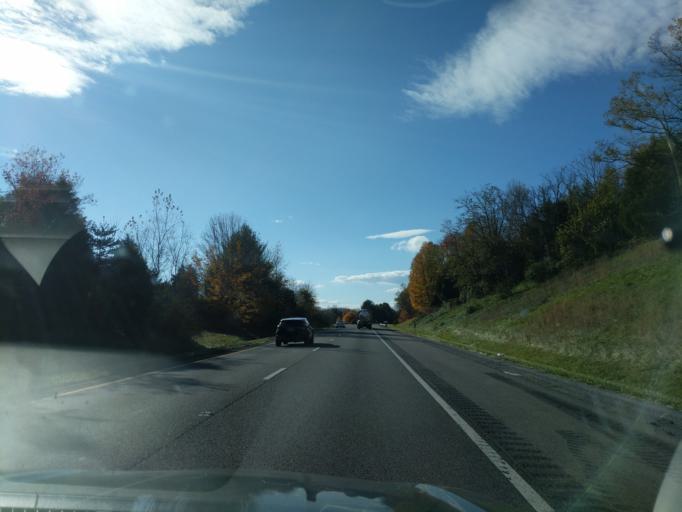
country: US
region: Virginia
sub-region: City of Radford
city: Radford
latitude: 37.0872
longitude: -80.6144
